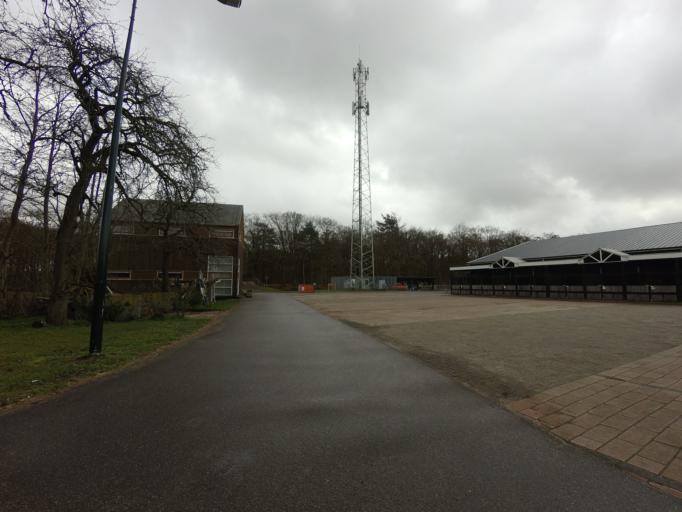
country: NL
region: Friesland
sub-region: Gemeente Gaasterlan-Sleat
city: Oudemirdum
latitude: 52.8730
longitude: 5.5382
